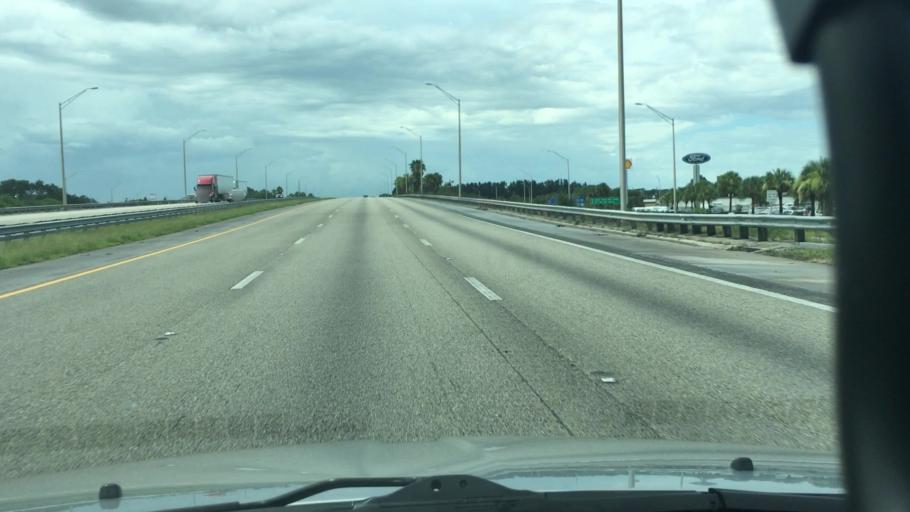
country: US
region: Florida
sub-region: Brevard County
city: Palm Bay
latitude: 27.9955
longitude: -80.6282
